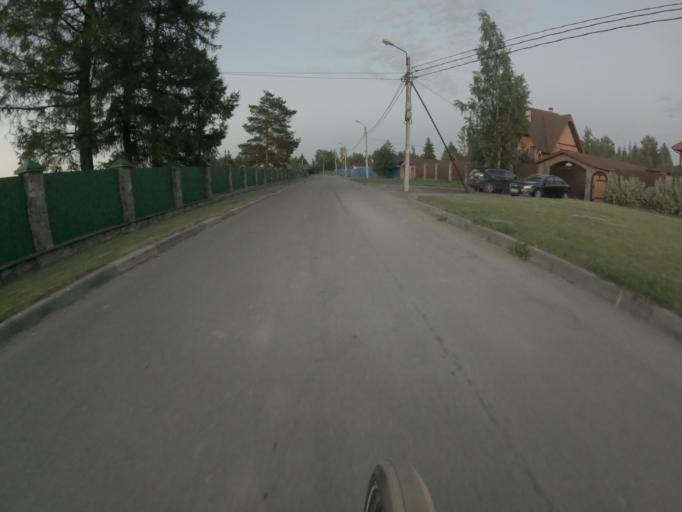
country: RU
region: St.-Petersburg
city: Sapernyy
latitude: 59.7828
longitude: 30.6775
